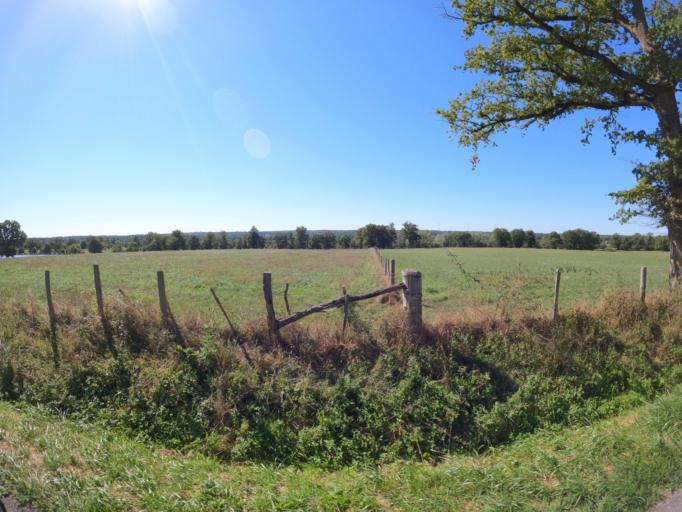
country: FR
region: Limousin
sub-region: Departement de la Haute-Vienne
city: Le Dorat
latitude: 46.2258
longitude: 1.0672
